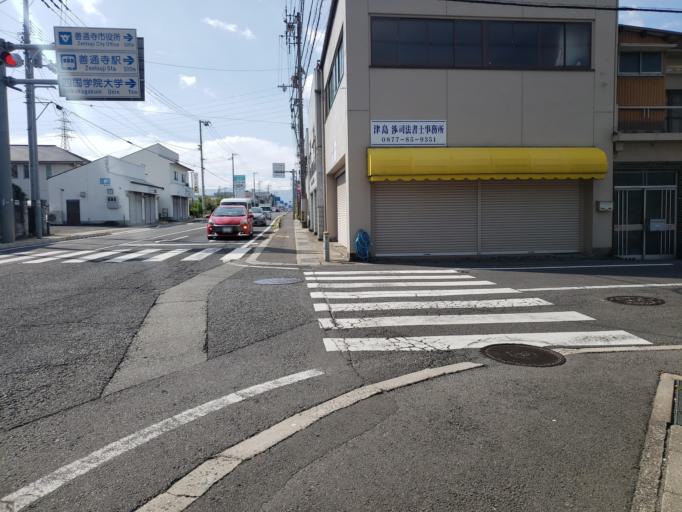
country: JP
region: Kagawa
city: Marugame
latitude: 34.2316
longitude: 133.7904
